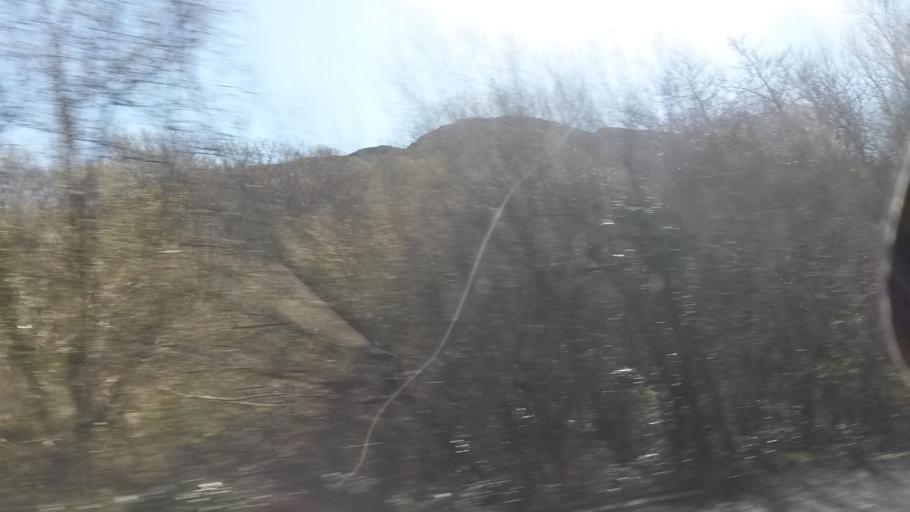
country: IE
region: Munster
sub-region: Ciarrai
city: Cill Airne
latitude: 51.9519
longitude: -9.3889
